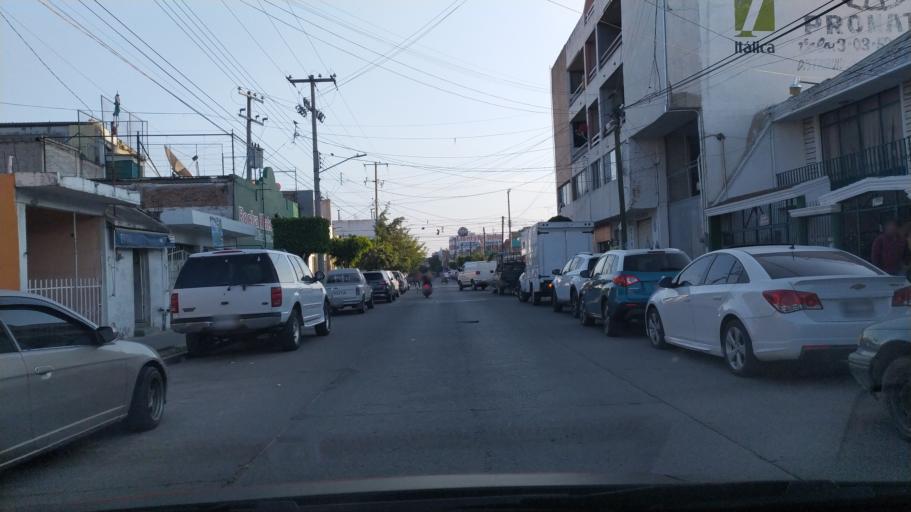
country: MX
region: Guanajuato
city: San Francisco del Rincon
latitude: 21.0133
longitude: -101.8563
